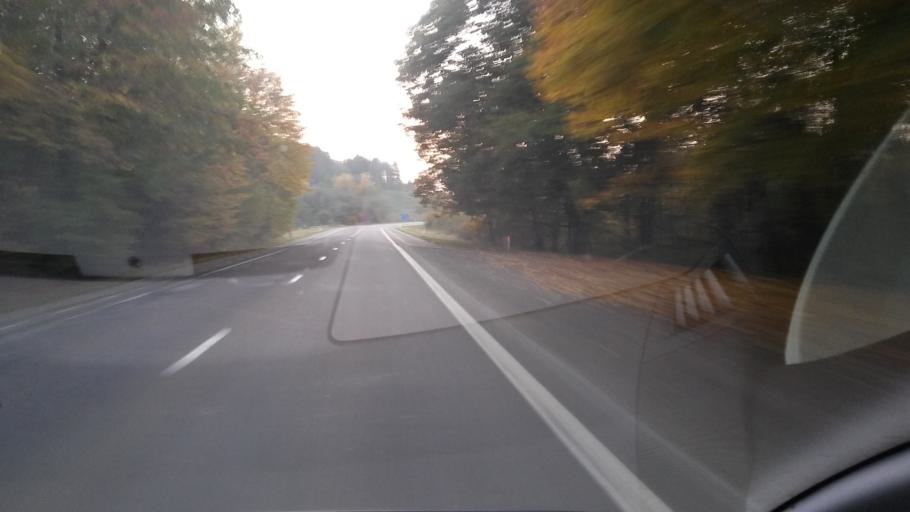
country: BE
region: Wallonia
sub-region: Province du Luxembourg
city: Saint-Leger
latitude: 49.6727
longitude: 5.6930
